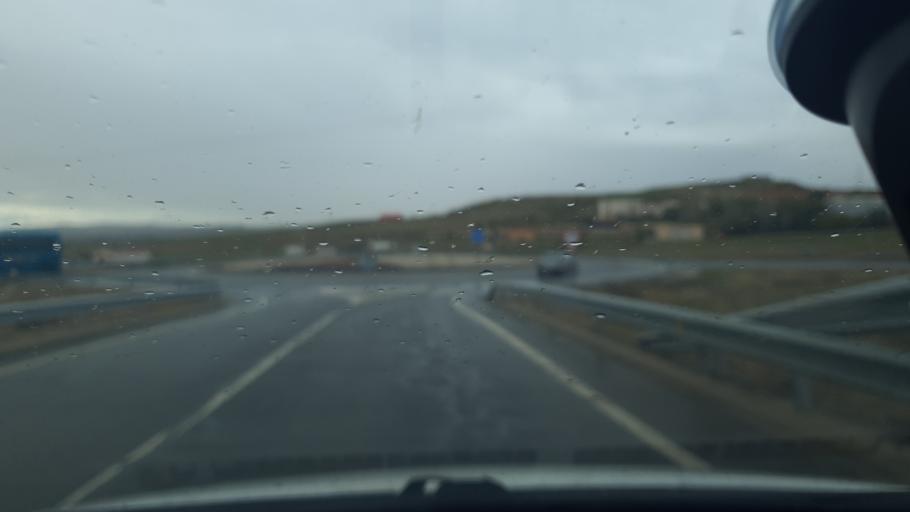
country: ES
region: Castille and Leon
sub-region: Provincia de Segovia
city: Carbonero el Mayor
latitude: 41.1117
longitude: -4.2549
